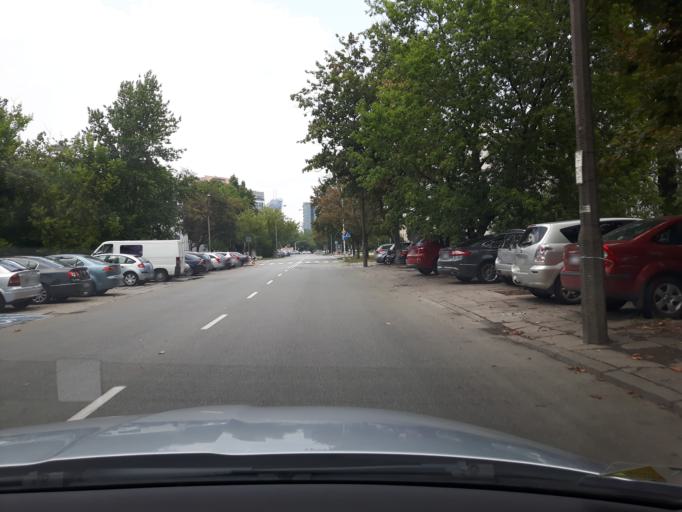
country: PL
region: Masovian Voivodeship
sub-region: Warszawa
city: Ochota
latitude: 52.2170
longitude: 20.9715
